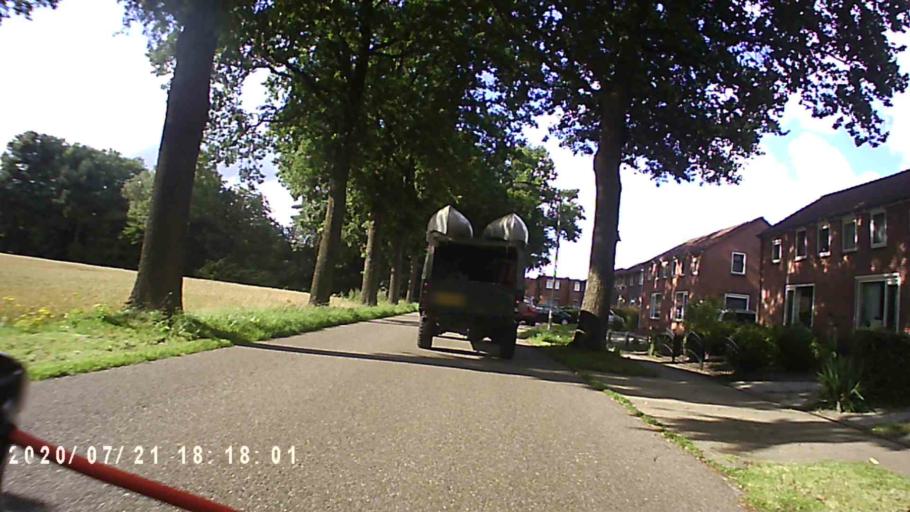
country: NL
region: Groningen
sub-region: Gemeente Hoogezand-Sappemeer
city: Hoogezand
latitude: 53.1818
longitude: 6.7548
